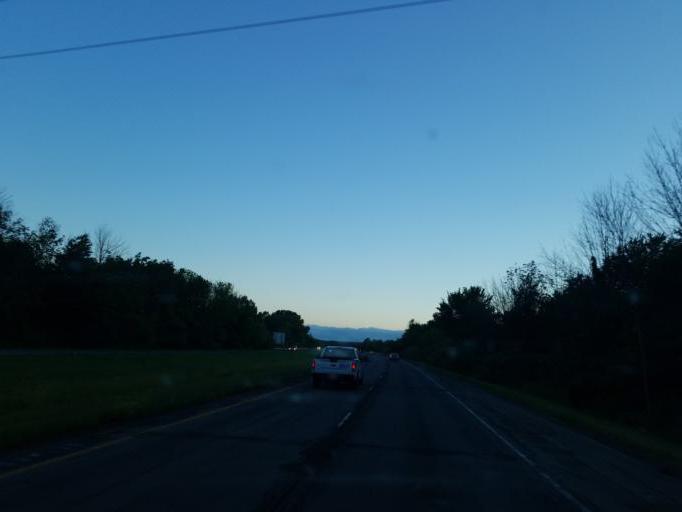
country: US
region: Ohio
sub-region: Summit County
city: Norton
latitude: 41.0091
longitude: -81.6621
